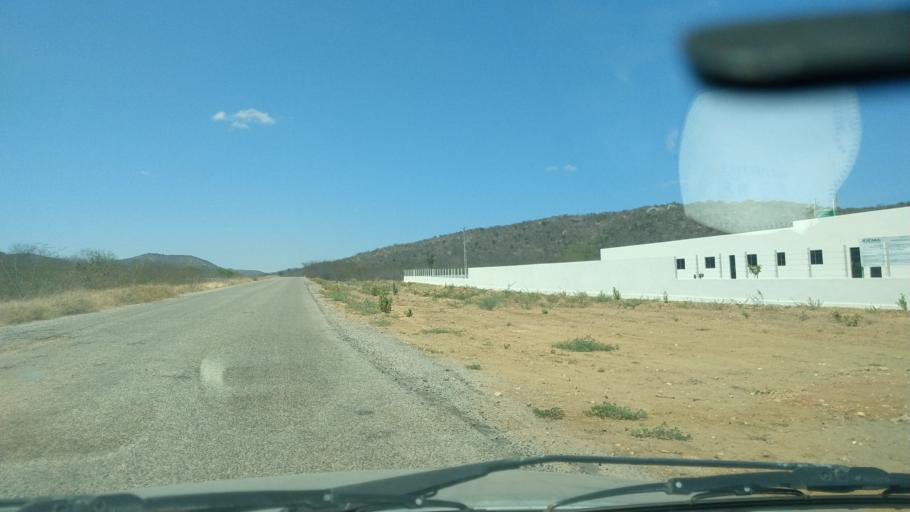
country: BR
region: Rio Grande do Norte
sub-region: Sao Tome
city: Sao Tome
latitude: -5.9737
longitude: -36.1373
